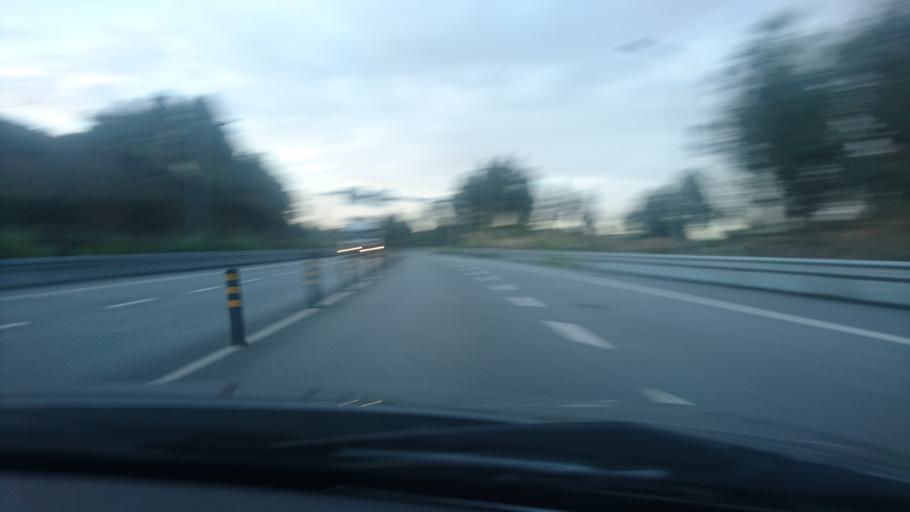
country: PT
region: Aveiro
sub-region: Santa Maria da Feira
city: Arrifana
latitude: 40.9226
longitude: -8.4899
